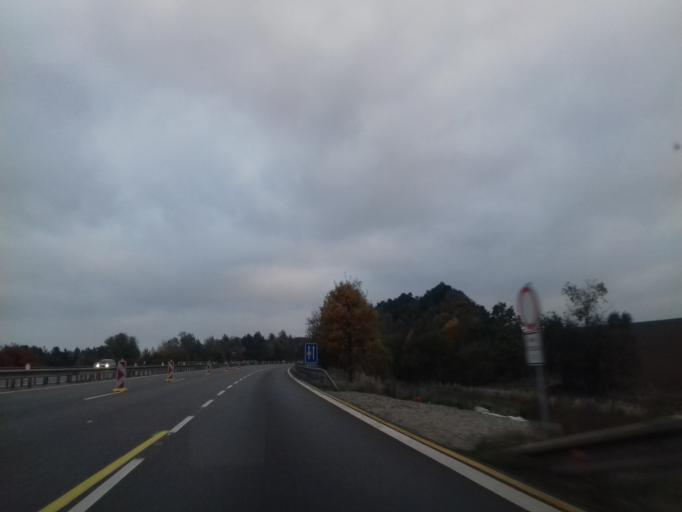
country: CZ
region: Central Bohemia
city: Trhovy Stepanov
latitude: 49.7403
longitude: 15.0381
